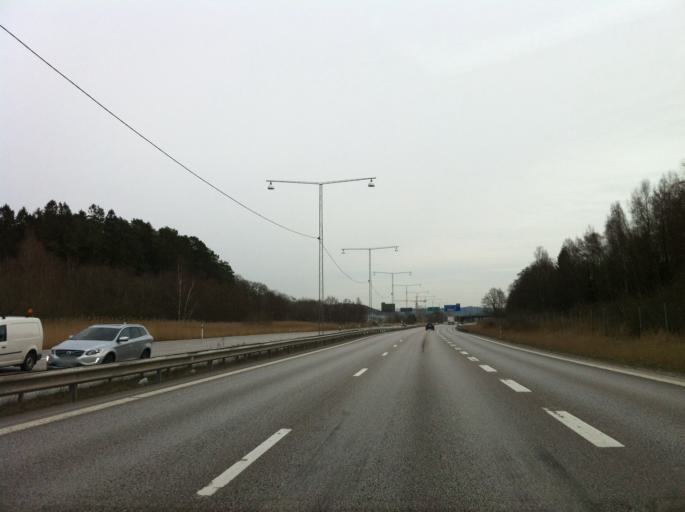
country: SE
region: Vaestra Goetaland
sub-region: Kungalvs Kommun
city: Kode
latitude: 57.9141
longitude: 11.8892
